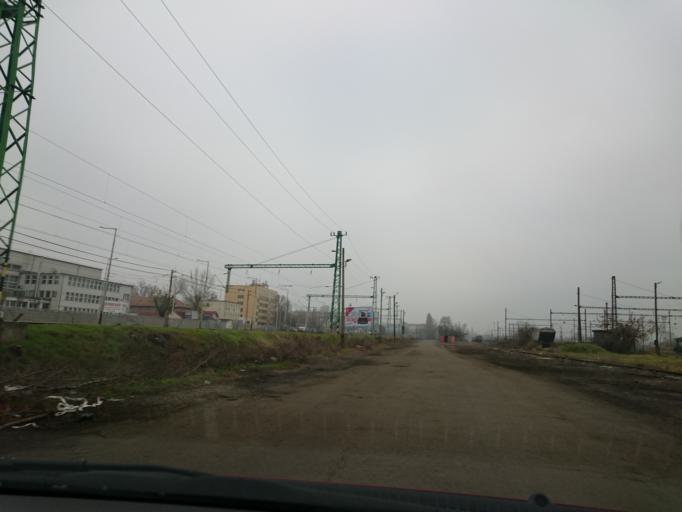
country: HU
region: Budapest
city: Budapest XX. keruelet
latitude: 47.4528
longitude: 19.0873
